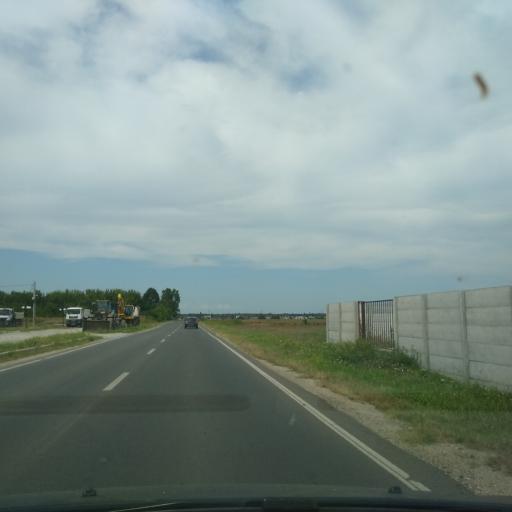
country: RO
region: Ilfov
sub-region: Comuna Balotesti
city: Balotesti
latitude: 44.6050
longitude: 26.1307
